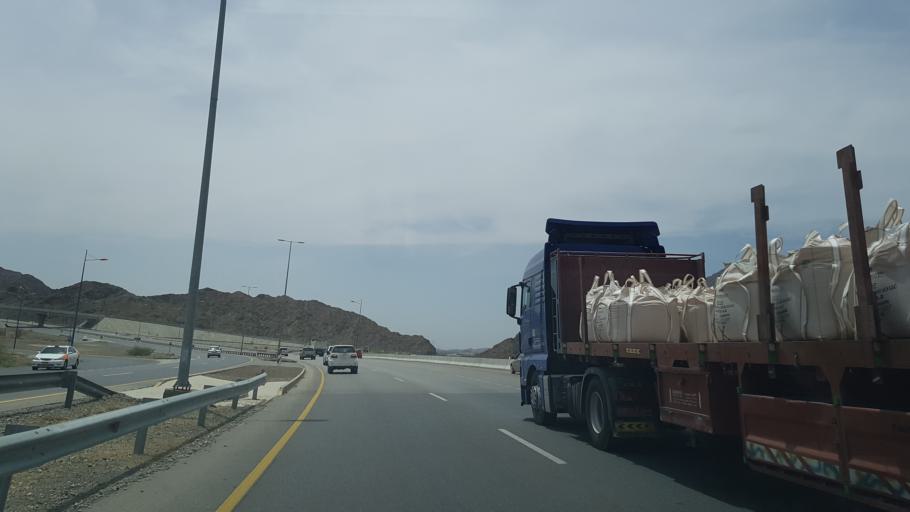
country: OM
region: Muhafazat ad Dakhiliyah
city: Izki
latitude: 22.9756
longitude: 57.7809
